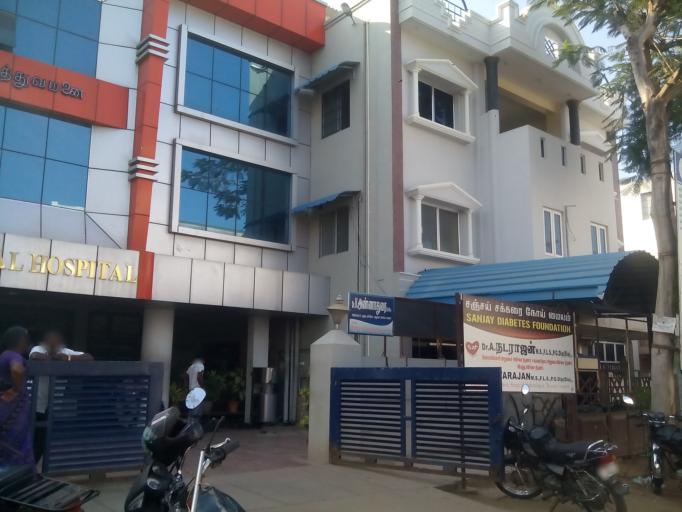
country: IN
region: Tamil Nadu
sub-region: Dindigul
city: Palani
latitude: 10.4541
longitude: 77.5140
